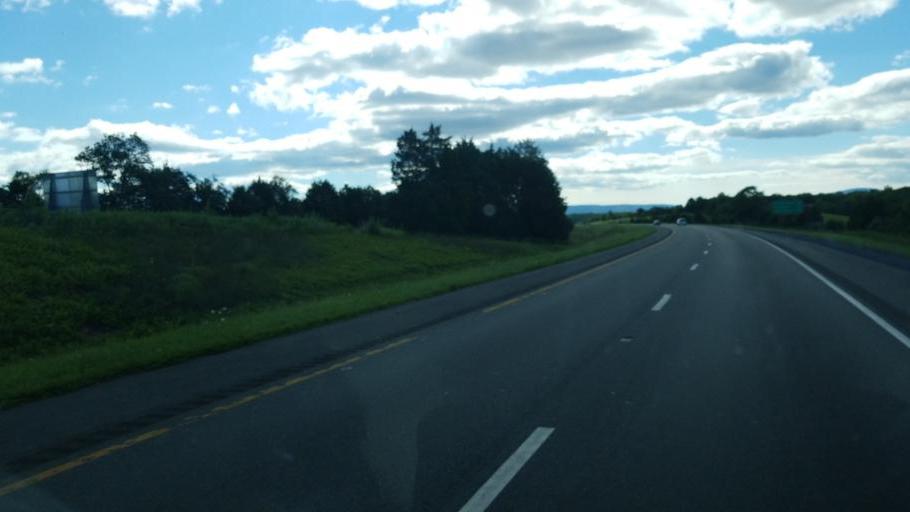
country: US
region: Virginia
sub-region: Frederick County
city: Middletown
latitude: 39.0024
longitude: -78.2873
